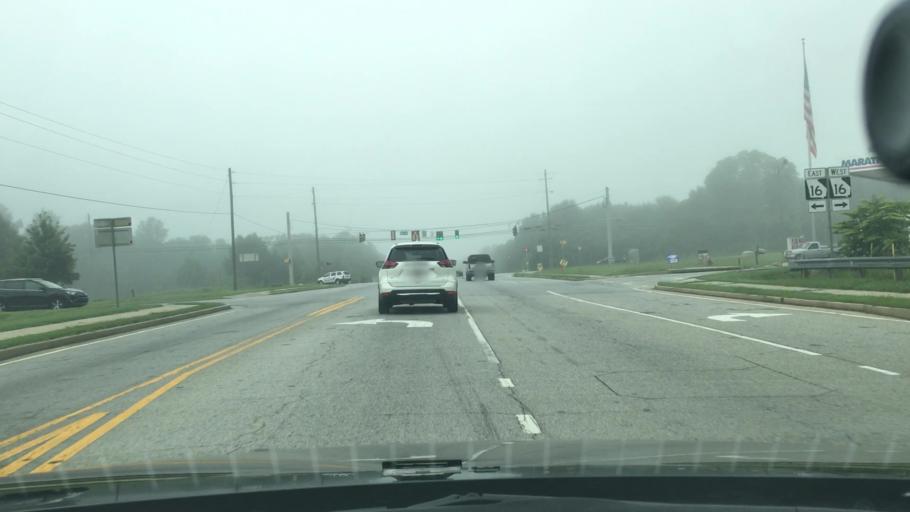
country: US
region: Georgia
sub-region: Coweta County
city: Senoia
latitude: 33.2942
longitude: -84.5438
